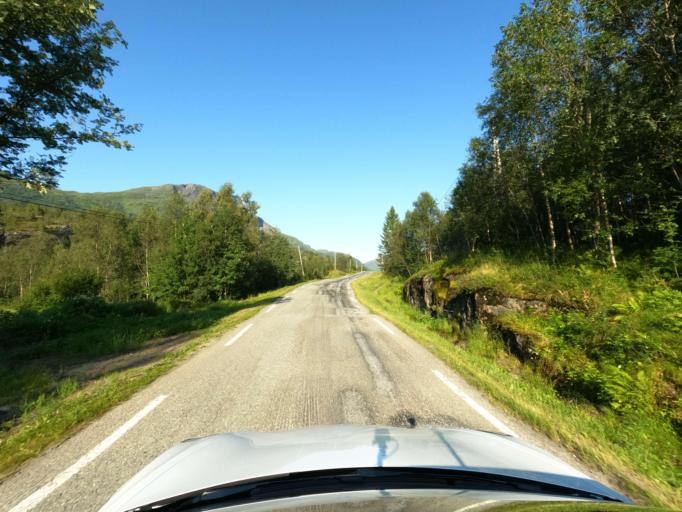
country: NO
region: Nordland
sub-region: Narvik
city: Bjerkvik
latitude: 68.5583
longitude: 17.6476
